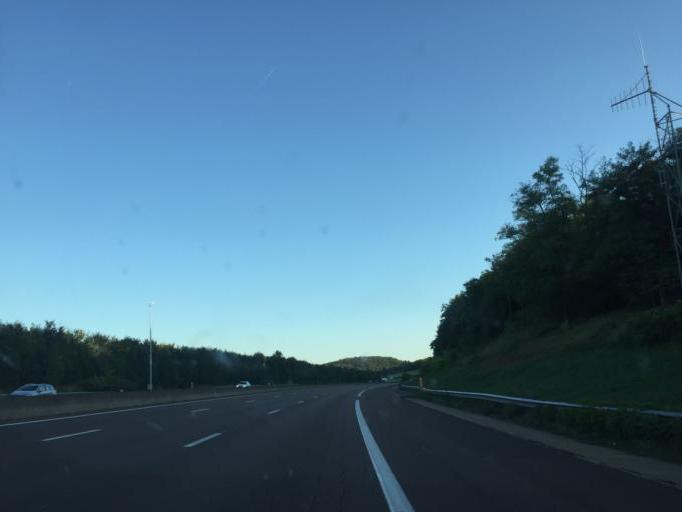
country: FR
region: Bourgogne
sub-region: Departement de Saone-et-Loire
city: Sennecey-le-Grand
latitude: 46.6313
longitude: 4.8603
